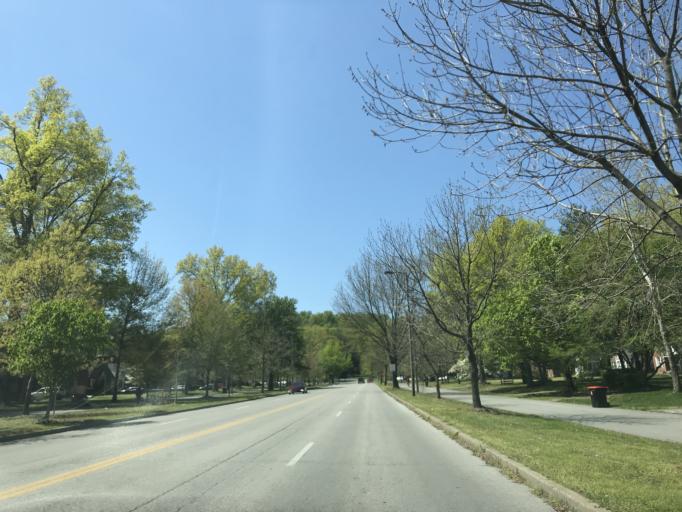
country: US
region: Kentucky
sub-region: Jefferson County
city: Shively
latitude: 38.1715
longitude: -85.7792
